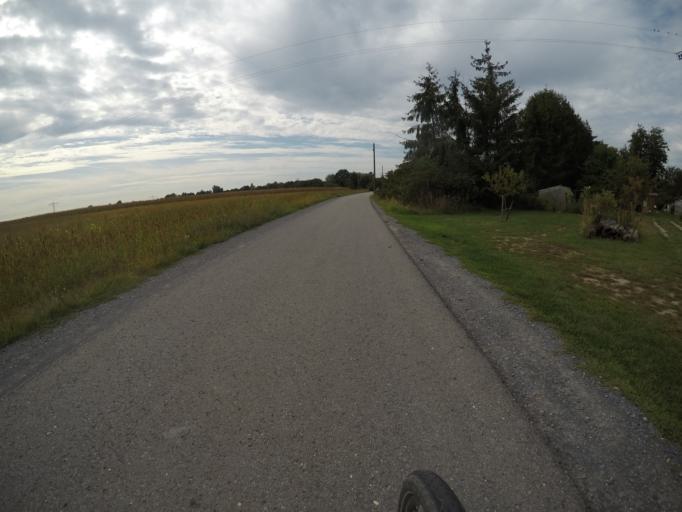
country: DE
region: Baden-Wuerttemberg
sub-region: Karlsruhe Region
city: Sankt Leon-Rot
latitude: 49.2524
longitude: 8.6300
